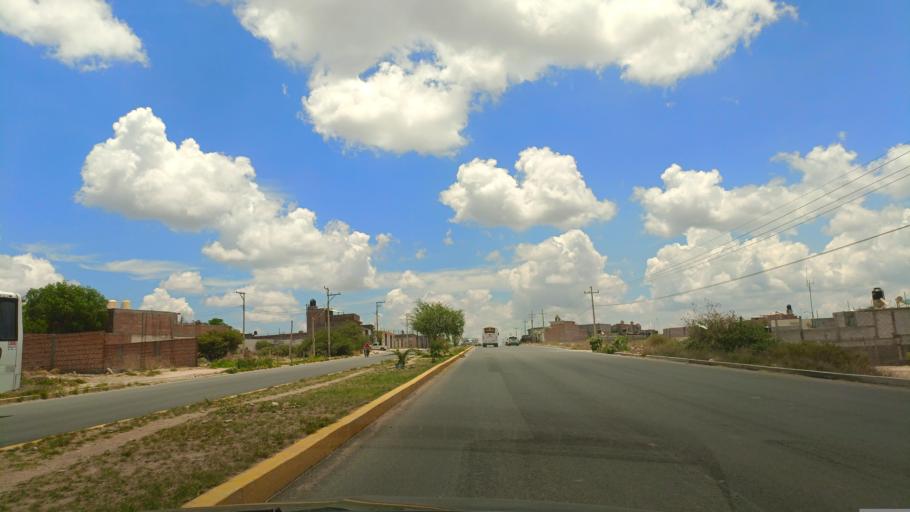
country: MX
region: Guerrero
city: San Luis de la Paz
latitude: 21.2894
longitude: -100.5022
